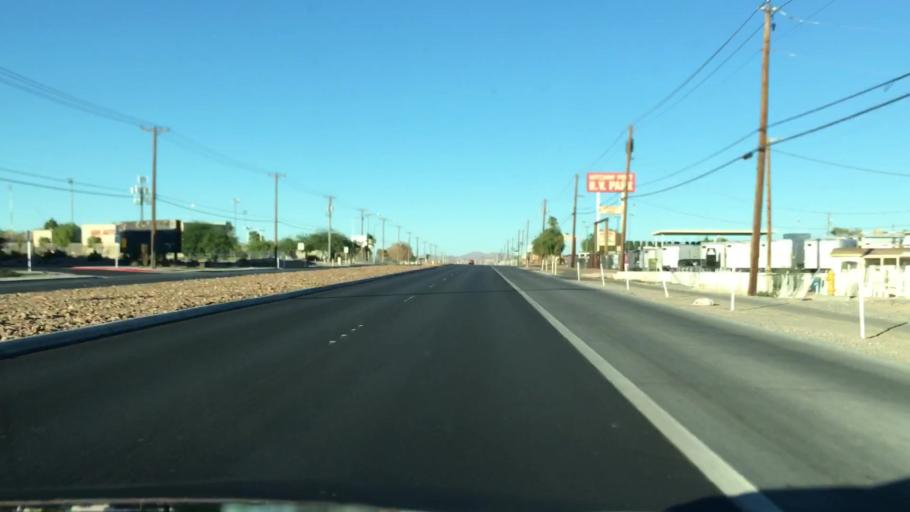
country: US
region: Nevada
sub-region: Clark County
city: Sunrise Manor
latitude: 36.2223
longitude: -115.0854
